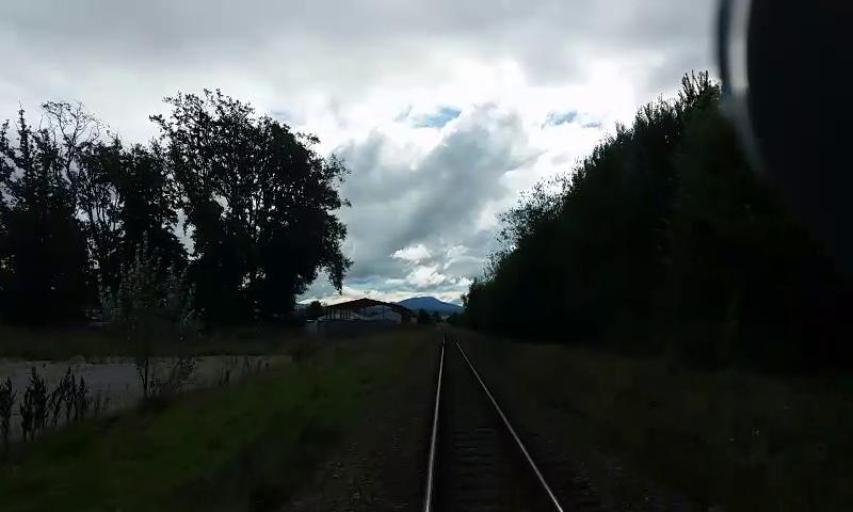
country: NZ
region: Canterbury
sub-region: Waimakariri District
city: Woodend
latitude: -43.3153
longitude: 172.6012
